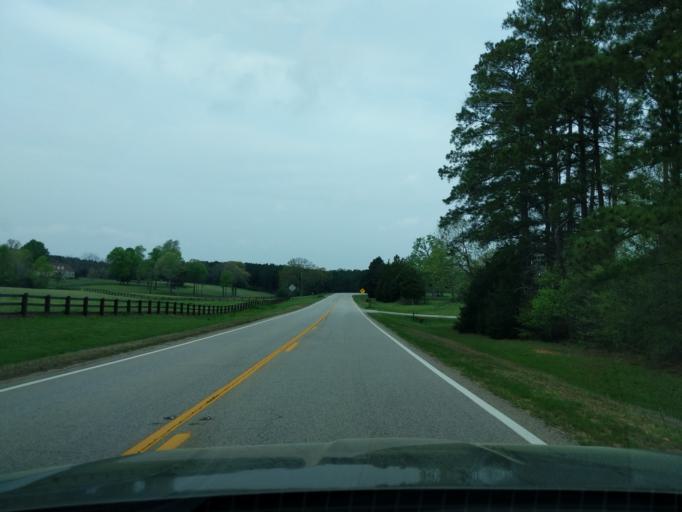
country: US
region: Georgia
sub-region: Lincoln County
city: Lincolnton
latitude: 33.7917
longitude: -82.3815
